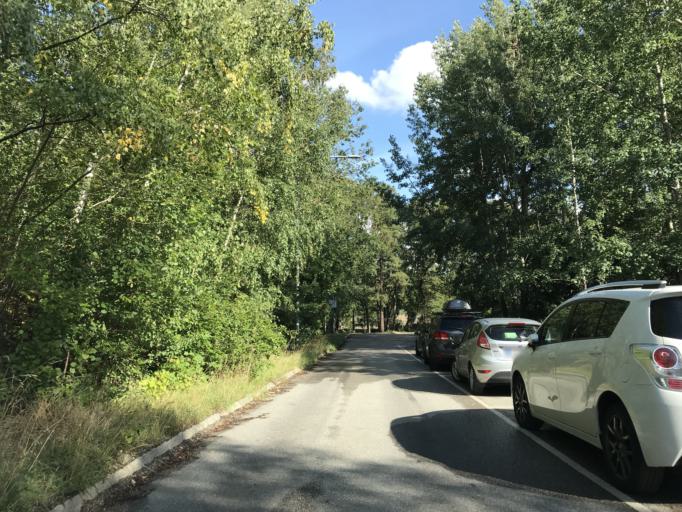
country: SE
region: Stockholm
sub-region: Stockholms Kommun
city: Arsta
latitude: 59.2863
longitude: 18.0160
